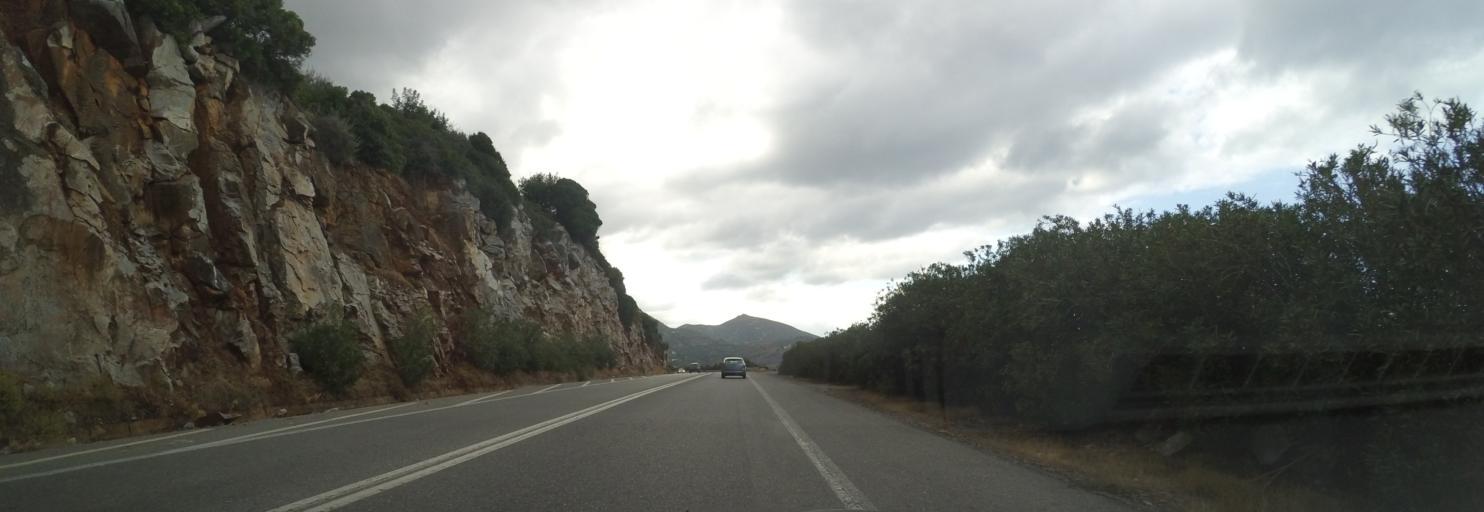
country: GR
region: Crete
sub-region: Nomos Rethymnis
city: Perama
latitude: 35.4091
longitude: 24.8037
